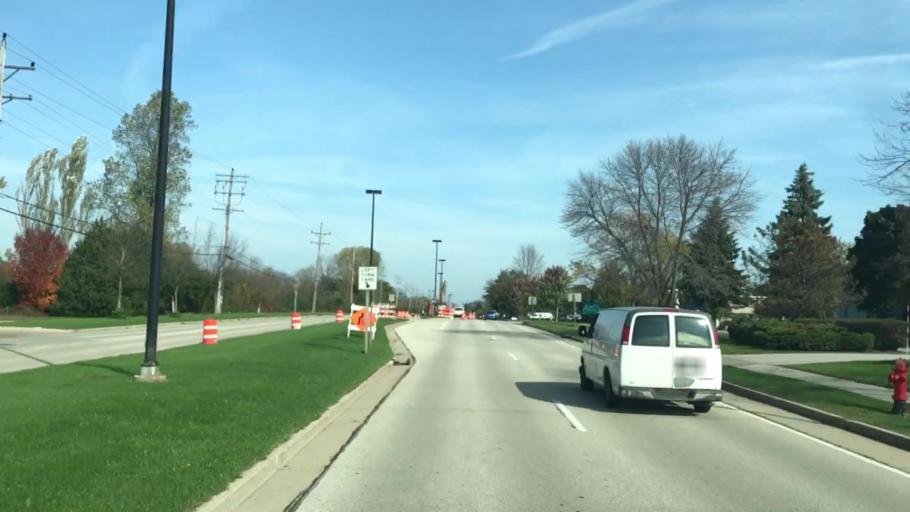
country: US
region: Wisconsin
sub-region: Milwaukee County
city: River Hills
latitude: 43.2004
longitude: -87.9243
